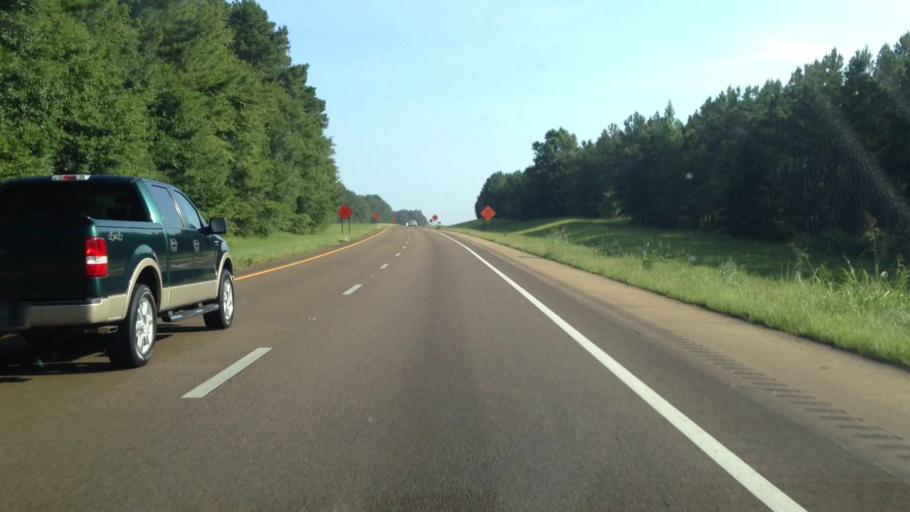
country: US
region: Mississippi
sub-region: Pike County
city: Summit
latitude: 31.4136
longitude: -90.4793
